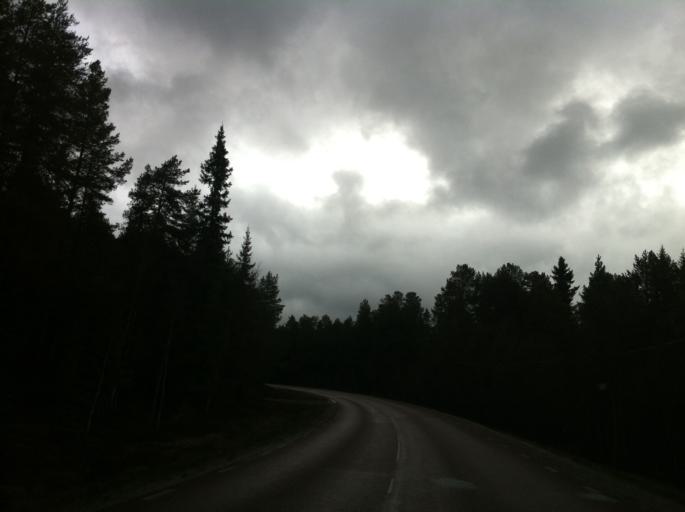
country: NO
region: Hedmark
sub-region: Engerdal
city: Engerdal
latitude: 62.4290
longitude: 12.7178
